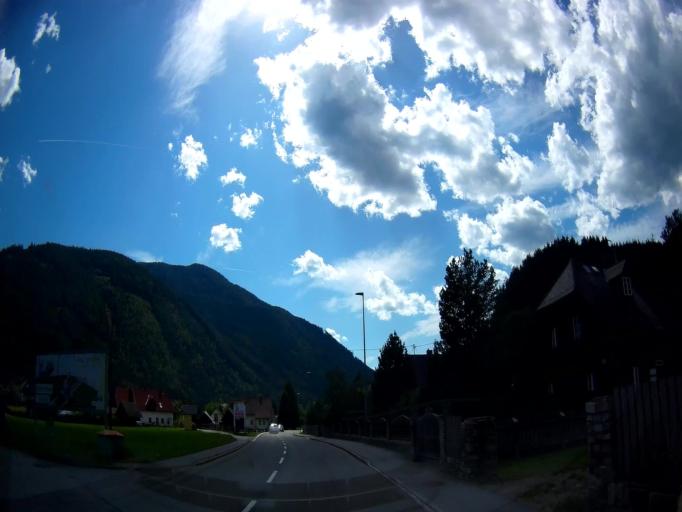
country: AT
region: Styria
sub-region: Politischer Bezirk Murau
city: Stadl an der Mur
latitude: 47.0852
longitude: 13.9748
